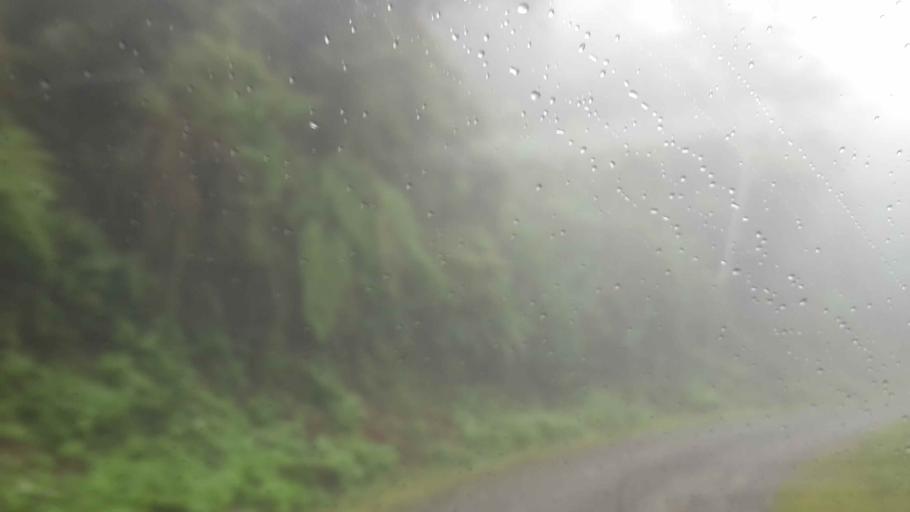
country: BO
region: Cochabamba
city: Colomi
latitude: -17.1002
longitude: -65.9817
